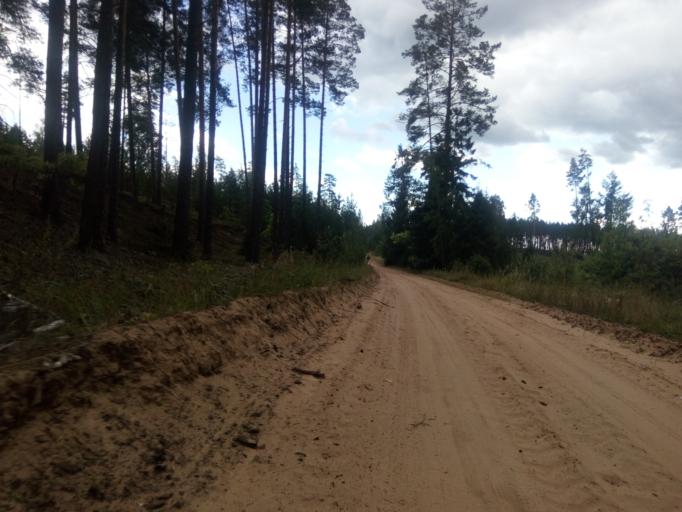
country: BY
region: Vitebsk
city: Dzisna
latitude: 55.6971
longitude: 28.3547
